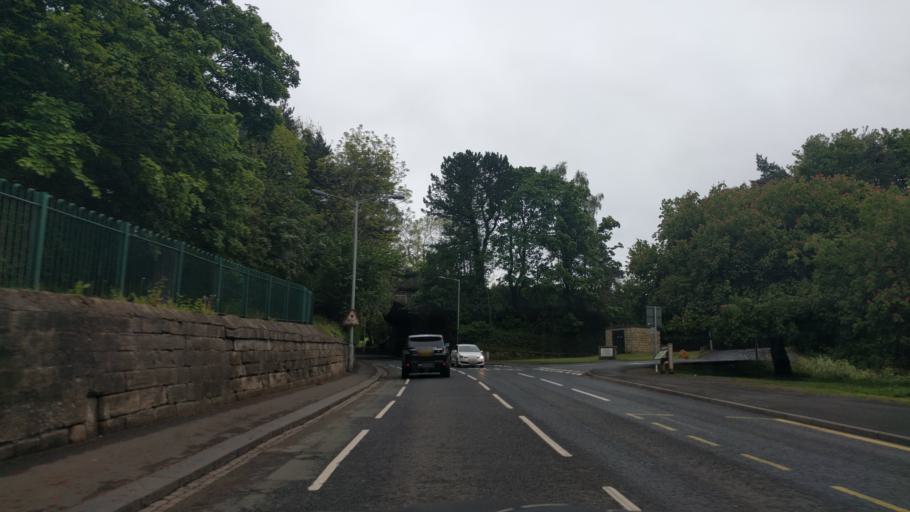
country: GB
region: England
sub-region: Northumberland
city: Morpeth
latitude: 55.1628
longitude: -1.6845
